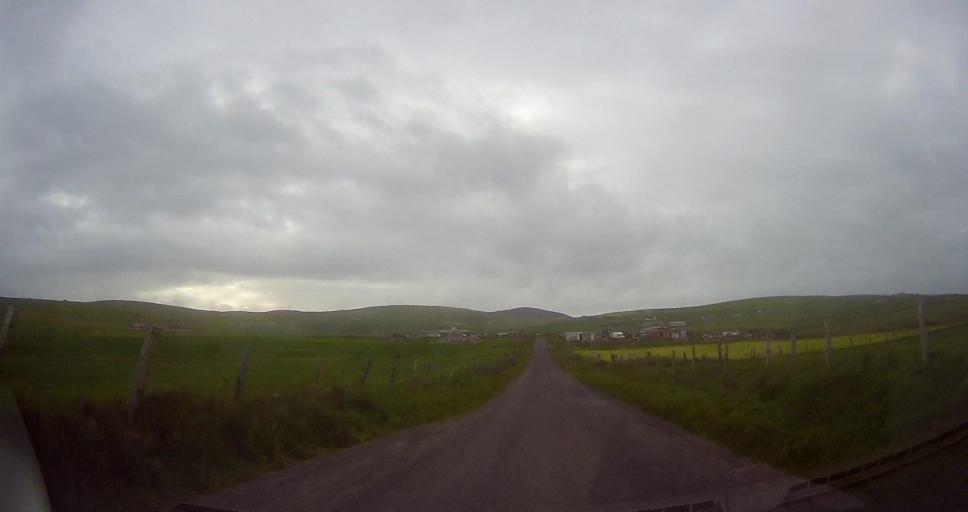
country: GB
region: Scotland
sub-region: Orkney Islands
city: Stromness
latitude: 58.9884
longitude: -3.2801
